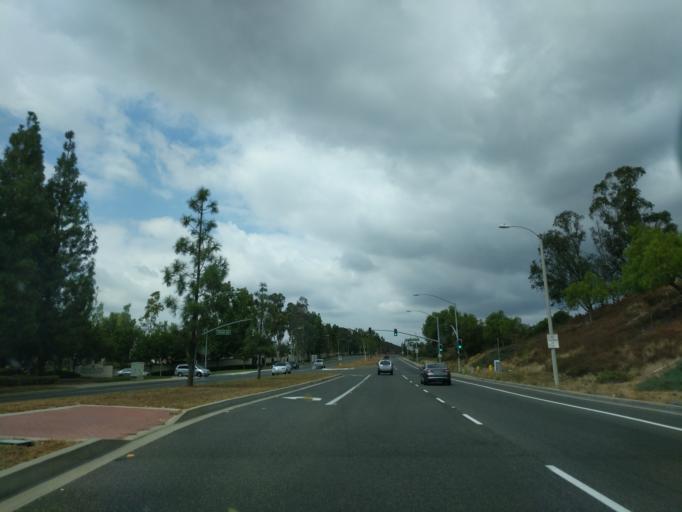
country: US
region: California
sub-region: Orange County
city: North Tustin
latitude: 33.7677
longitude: -117.7599
